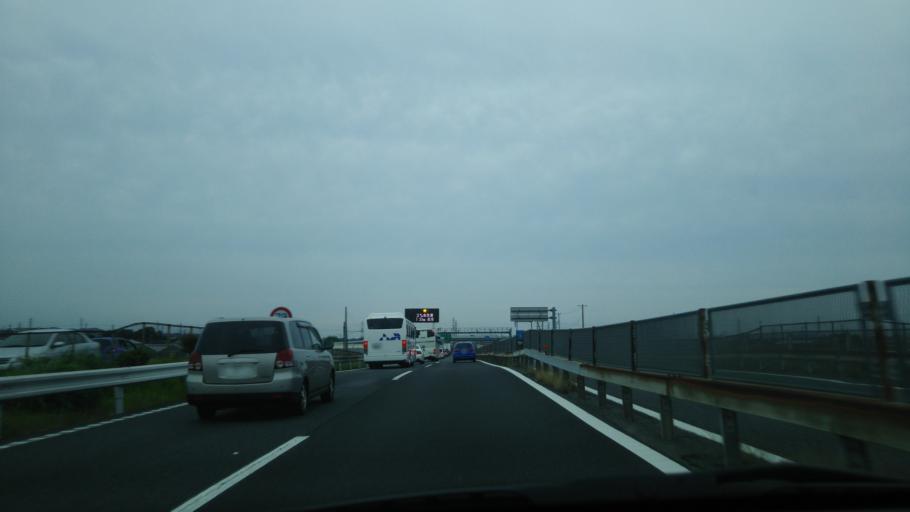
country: JP
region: Kanagawa
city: Isehara
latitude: 35.3815
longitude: 139.3296
